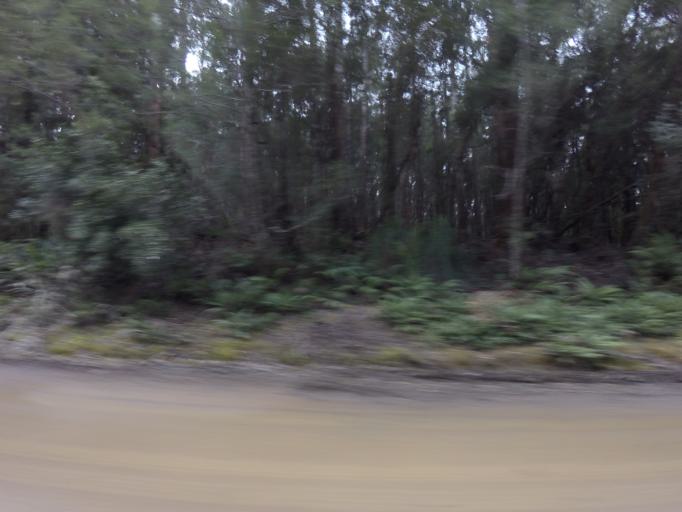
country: AU
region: Tasmania
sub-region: Huon Valley
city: Geeveston
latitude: -43.4026
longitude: 146.8645
